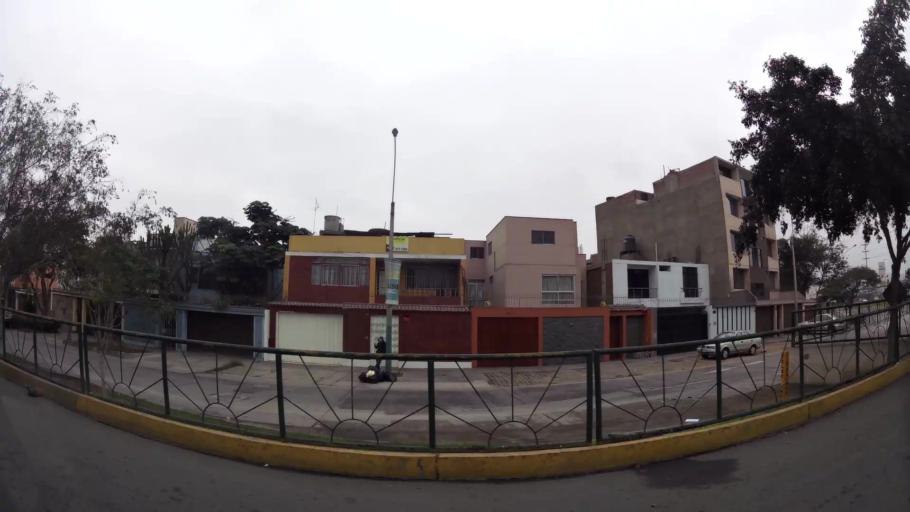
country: PE
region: Lima
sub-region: Lima
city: San Luis
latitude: -12.0835
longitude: -76.9851
